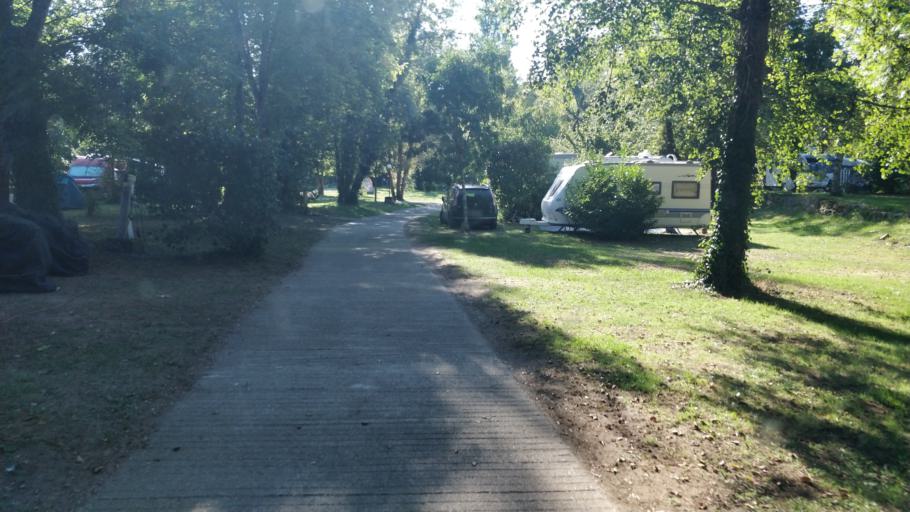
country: FR
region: Limousin
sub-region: Departement de la Correze
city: Beaulieu-sur-Dordogne
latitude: 44.9814
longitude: 1.8406
